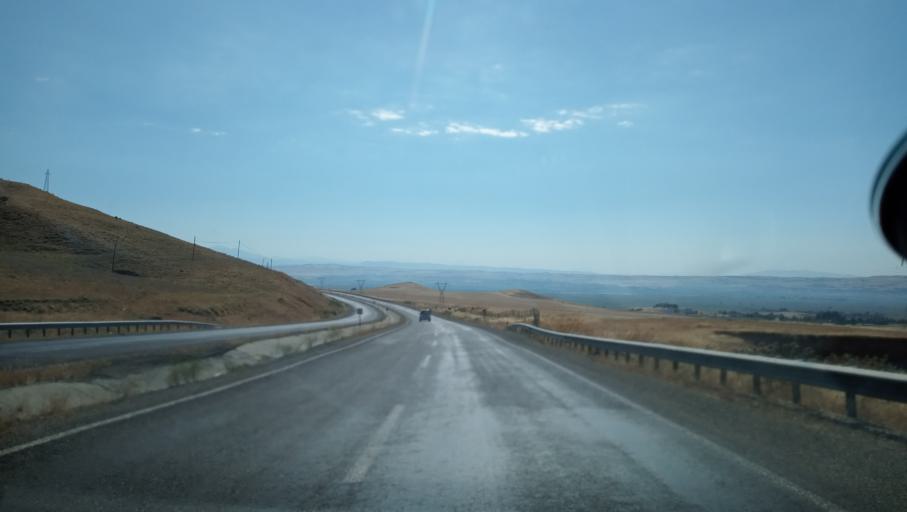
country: TR
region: Diyarbakir
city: Malabadi
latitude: 38.1181
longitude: 41.1376
